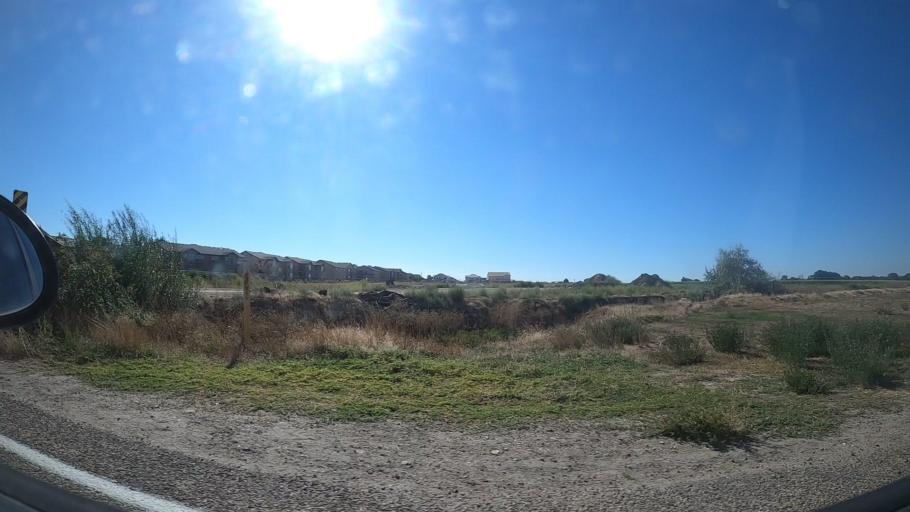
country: US
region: Idaho
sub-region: Canyon County
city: Nampa
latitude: 43.6025
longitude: -116.6133
